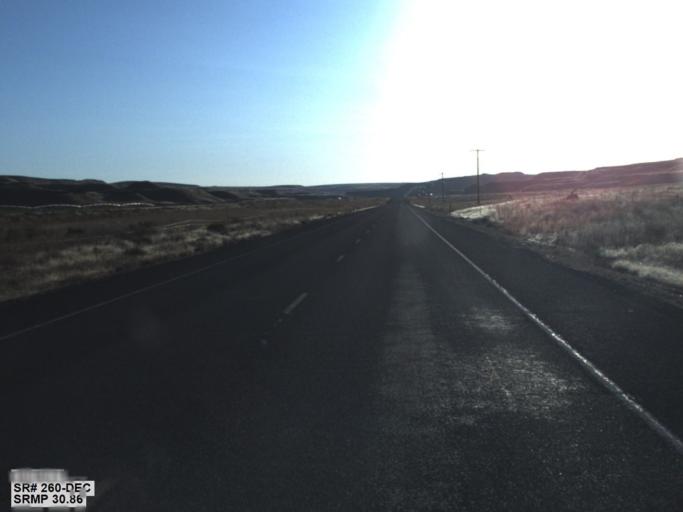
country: US
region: Washington
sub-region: Franklin County
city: Connell
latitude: 46.6811
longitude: -118.4477
